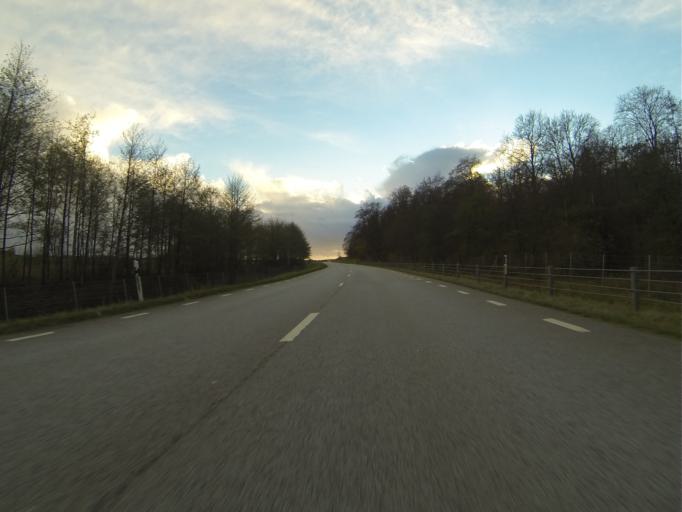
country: SE
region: Skane
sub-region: Trelleborgs Kommun
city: Anderslov
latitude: 55.5228
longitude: 13.3356
